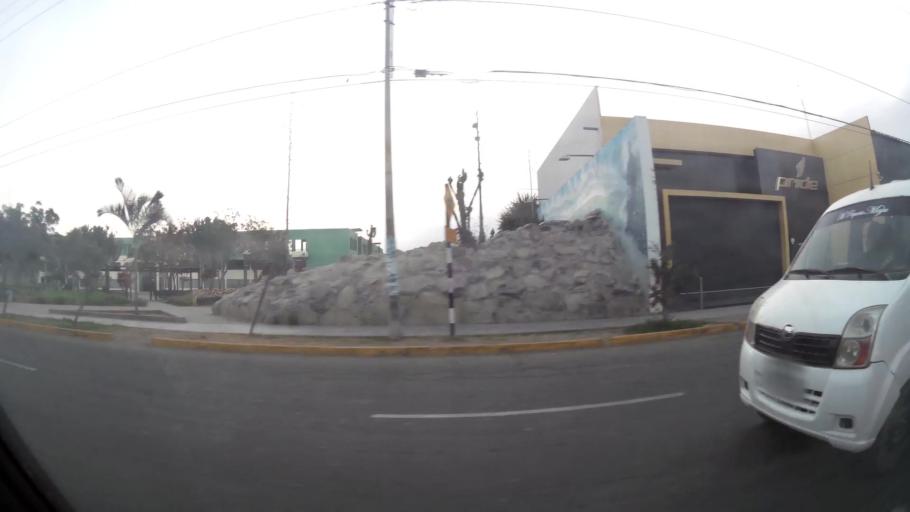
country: PE
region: La Libertad
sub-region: Provincia de Trujillo
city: Trujillo
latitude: -8.1120
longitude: -79.0481
